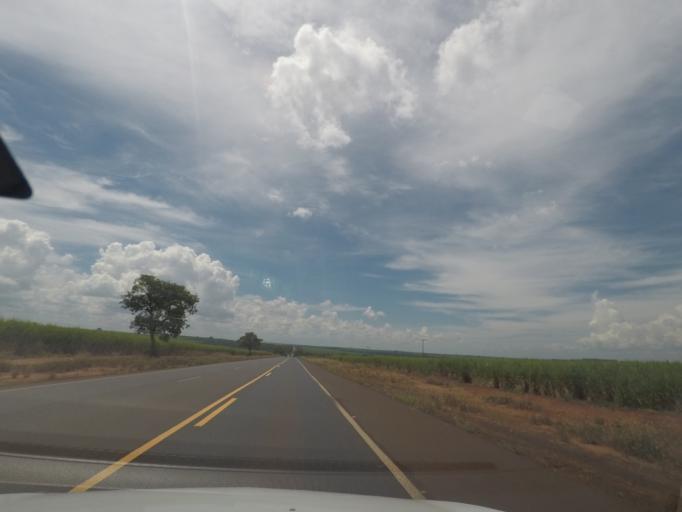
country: BR
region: Sao Paulo
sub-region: Barretos
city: Barretos
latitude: -20.2716
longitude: -48.6729
